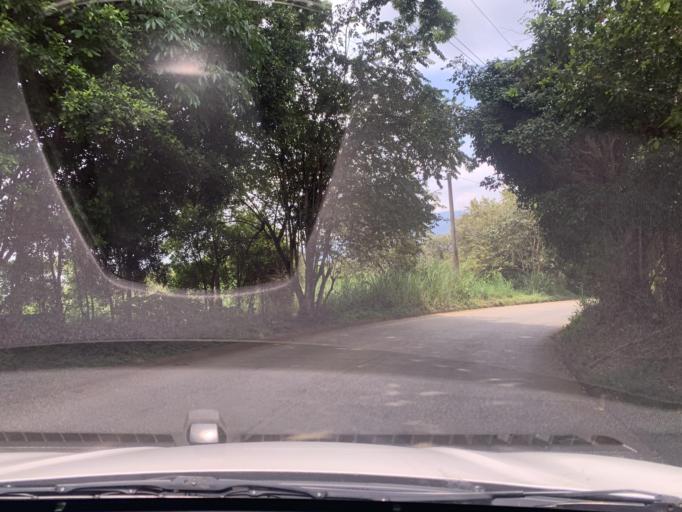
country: CO
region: Valle del Cauca
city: Jamundi
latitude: 3.3354
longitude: -76.5497
